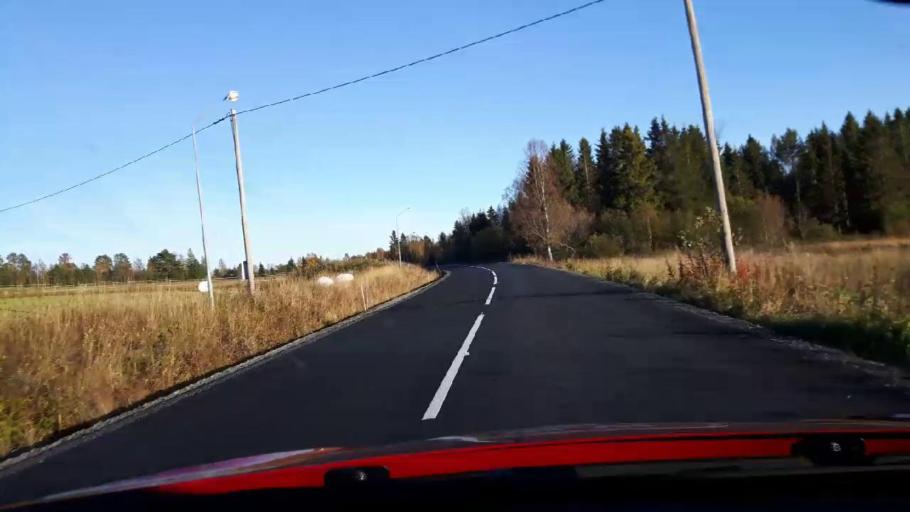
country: SE
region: Jaemtland
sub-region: OEstersunds Kommun
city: Lit
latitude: 63.4330
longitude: 14.8459
